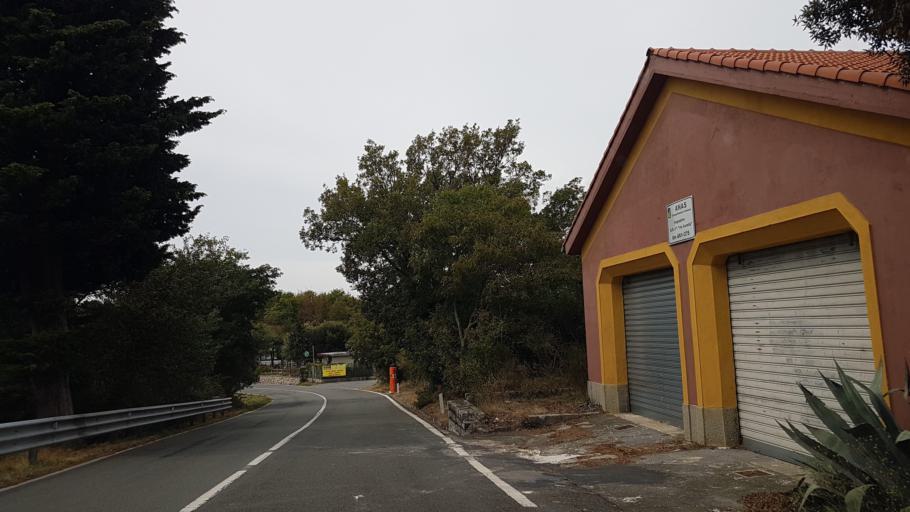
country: IT
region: Liguria
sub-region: Provincia di Genova
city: Castiglione
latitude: 44.2580
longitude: 9.5165
